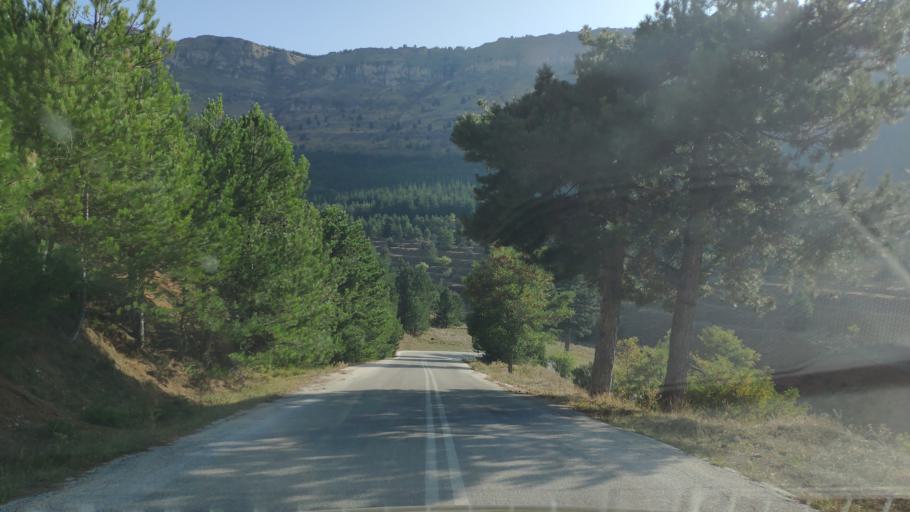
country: GR
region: West Greece
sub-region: Nomos Achaias
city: Aiyira
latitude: 38.0489
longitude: 22.3851
